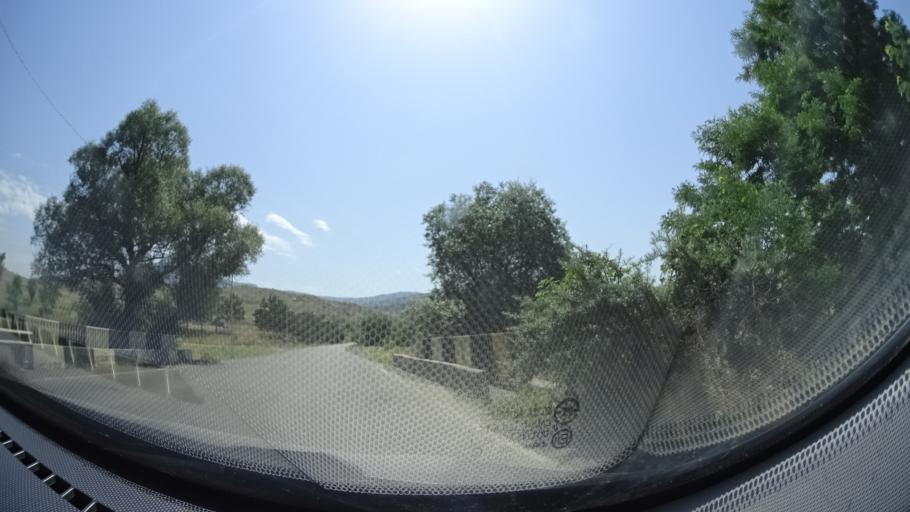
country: GE
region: Samtskhe-Javakheti
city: Aspindza
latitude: 41.5882
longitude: 43.2341
